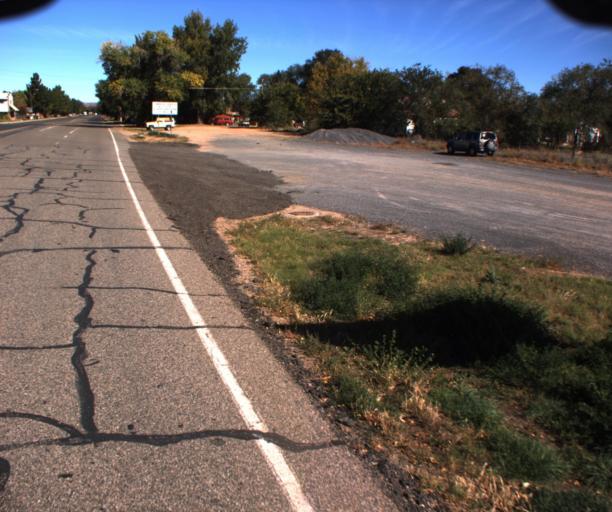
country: US
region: Arizona
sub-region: Coconino County
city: Fredonia
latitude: 36.9446
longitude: -112.5263
